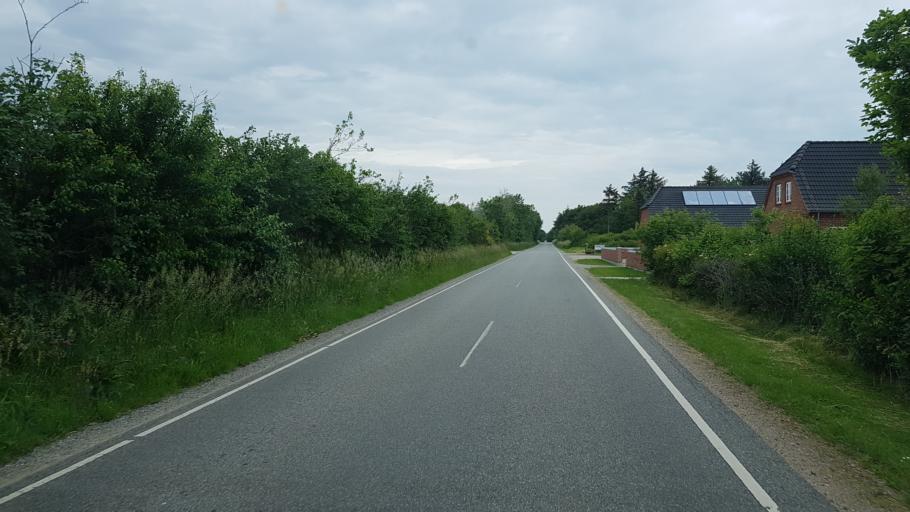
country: DK
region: South Denmark
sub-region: Varde Kommune
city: Oksbol
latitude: 55.6706
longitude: 8.3089
